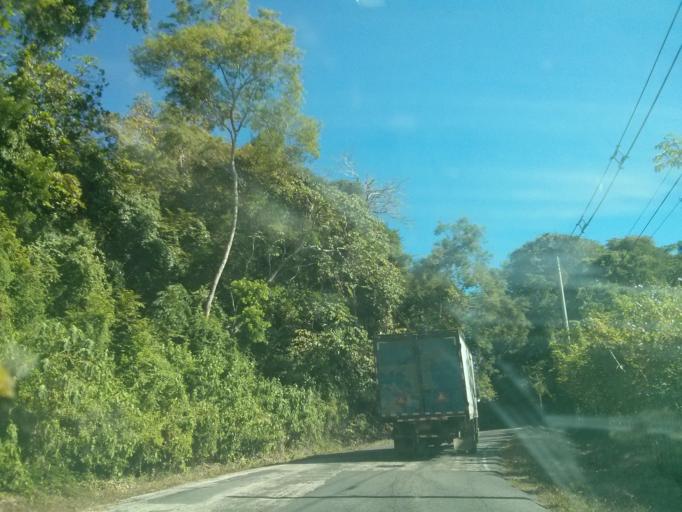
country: CR
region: Puntarenas
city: Paquera
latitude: 9.7908
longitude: -84.9412
